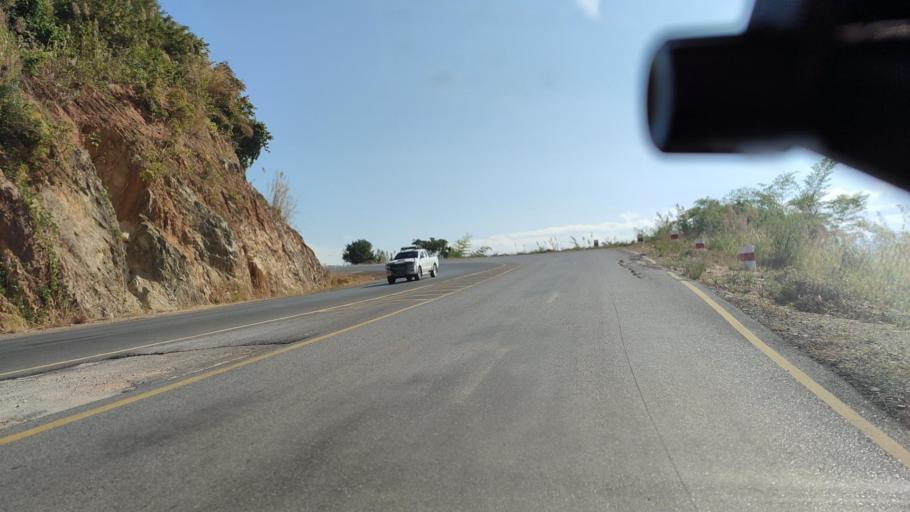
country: MM
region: Shan
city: Lashio
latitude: 23.3236
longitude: 97.9777
